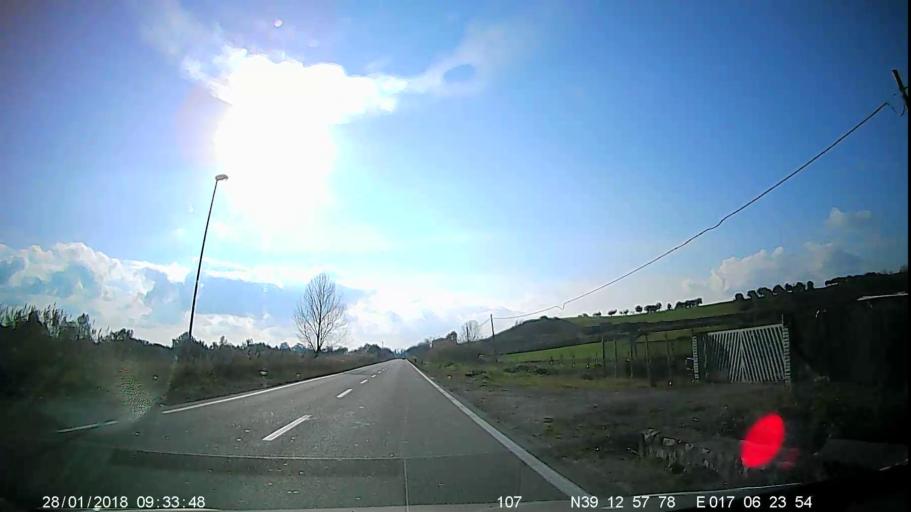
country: IT
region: Calabria
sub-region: Provincia di Crotone
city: Tronca
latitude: 39.2156
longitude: 17.1068
